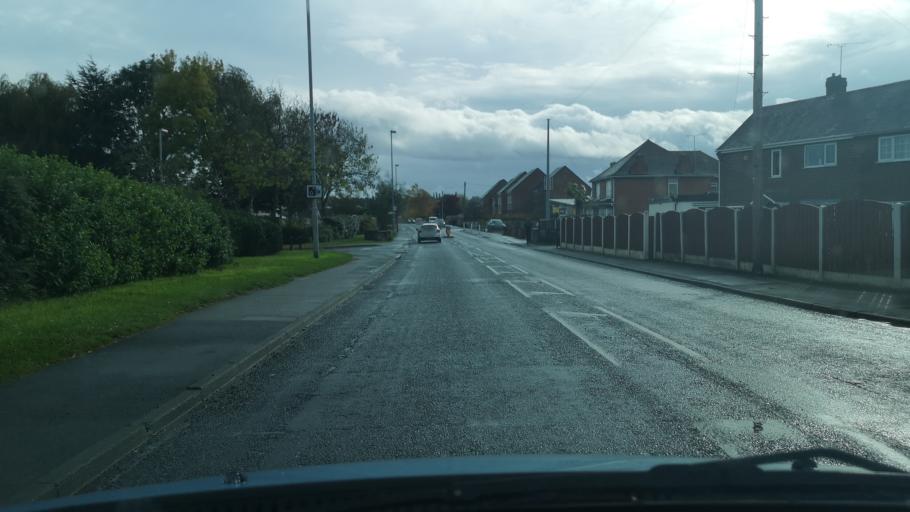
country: GB
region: England
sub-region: City and Borough of Wakefield
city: Fitzwilliam
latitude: 53.6273
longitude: -1.3708
